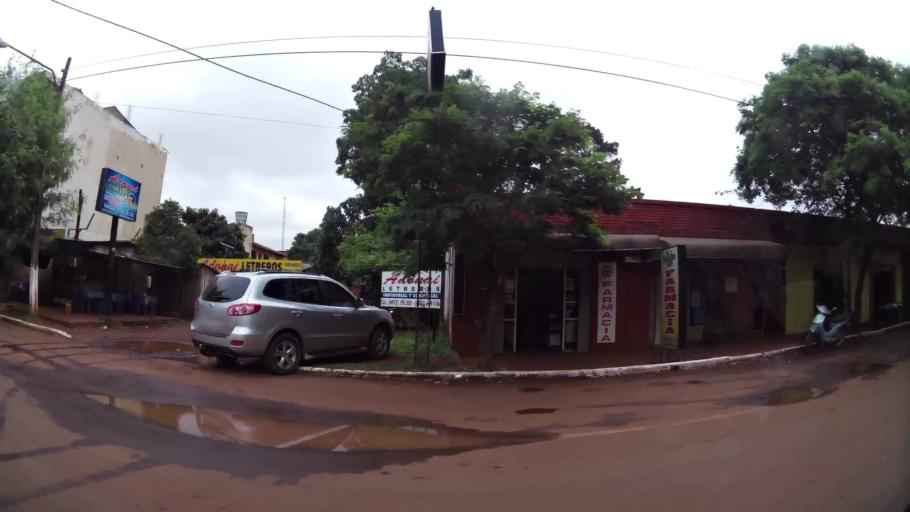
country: PY
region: Alto Parana
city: Ciudad del Este
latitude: -25.4834
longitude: -54.7624
